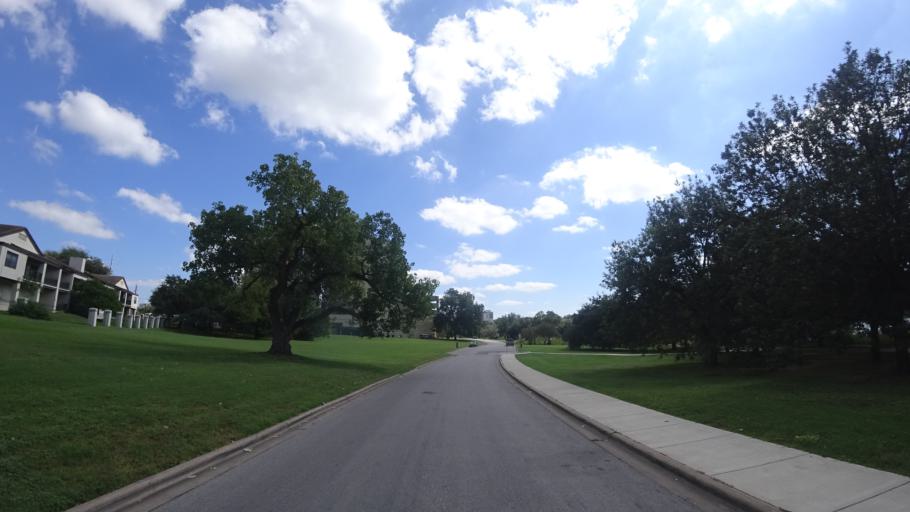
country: US
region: Texas
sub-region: Travis County
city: Austin
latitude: 30.2544
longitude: -97.7388
